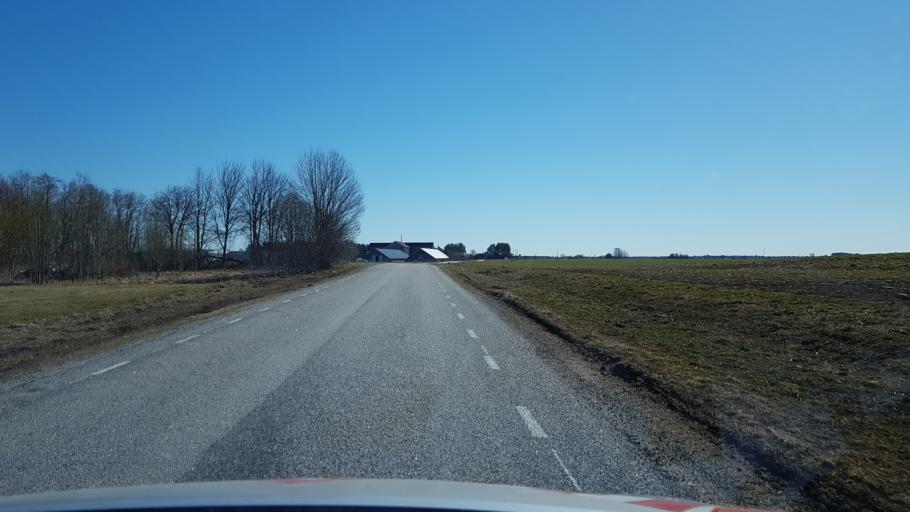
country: EE
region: Laeaene-Virumaa
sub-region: Haljala vald
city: Haljala
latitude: 59.4346
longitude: 26.2274
